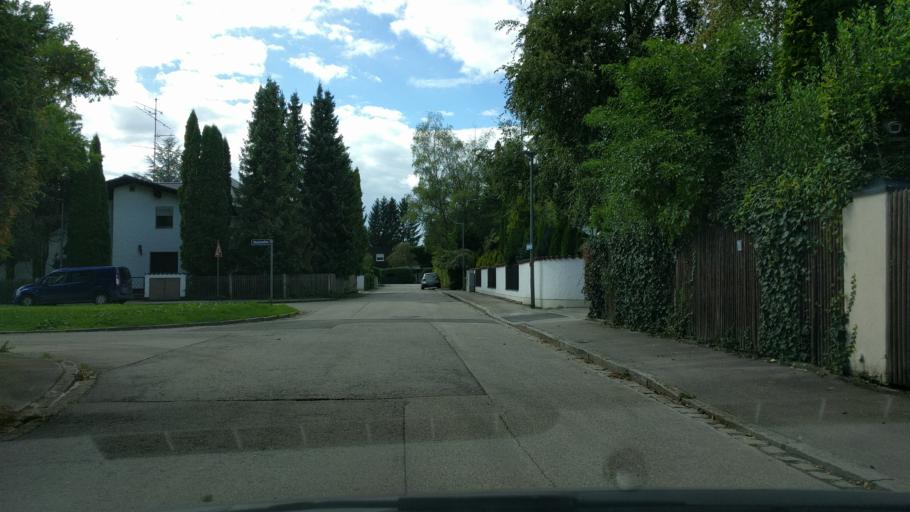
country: DE
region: Bavaria
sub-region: Upper Bavaria
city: Grunwald
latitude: 48.0438
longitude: 11.5354
